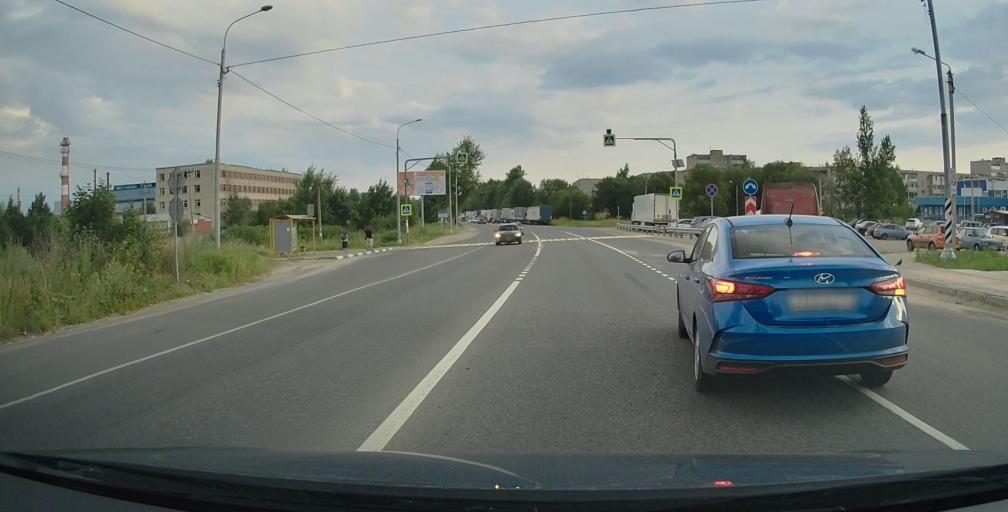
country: RU
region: Moskovskaya
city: Shemetovo
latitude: 56.4504
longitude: 38.0994
